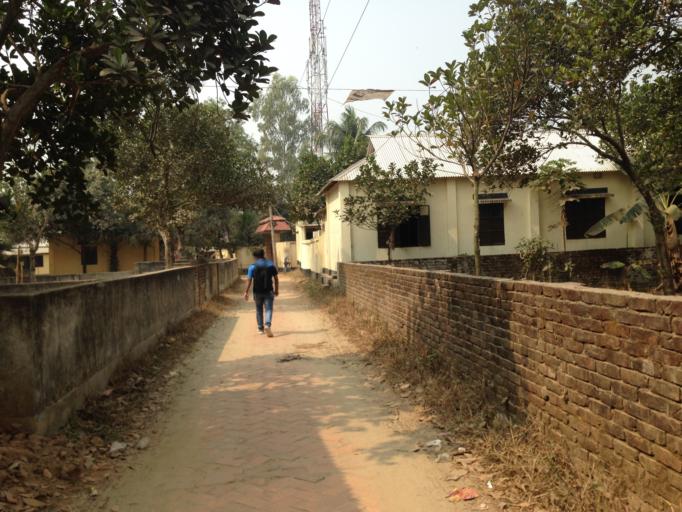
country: BD
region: Dhaka
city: Tungi
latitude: 23.8729
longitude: 90.3198
